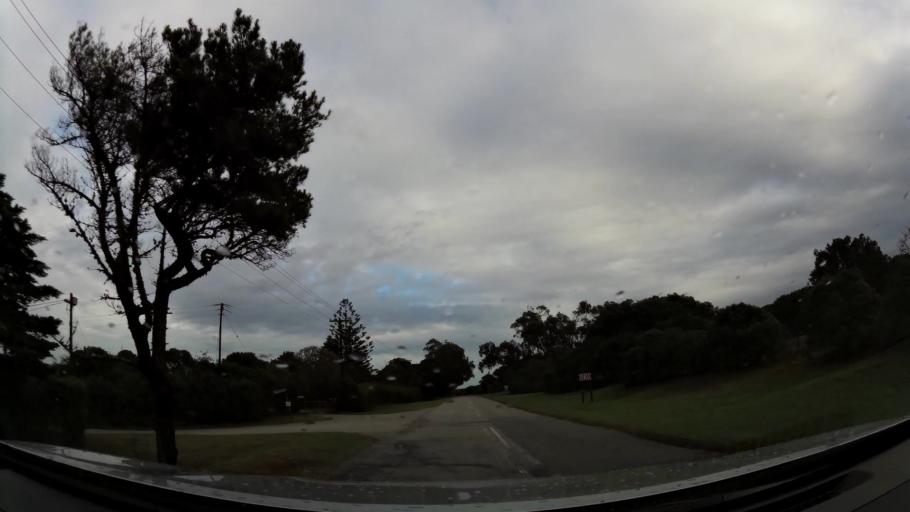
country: ZA
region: Eastern Cape
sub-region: Nelson Mandela Bay Metropolitan Municipality
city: Port Elizabeth
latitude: -34.0164
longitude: 25.5053
